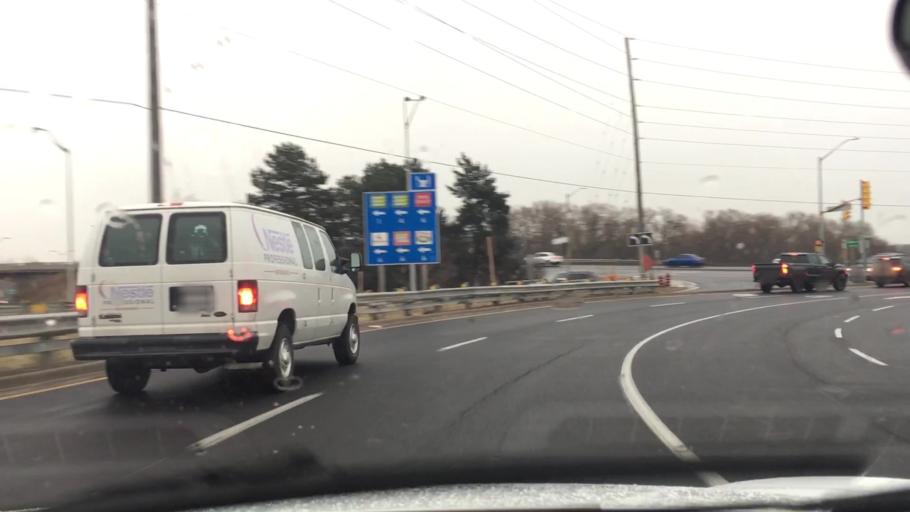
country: CA
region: Ontario
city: Oshawa
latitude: 43.8865
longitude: -78.8317
